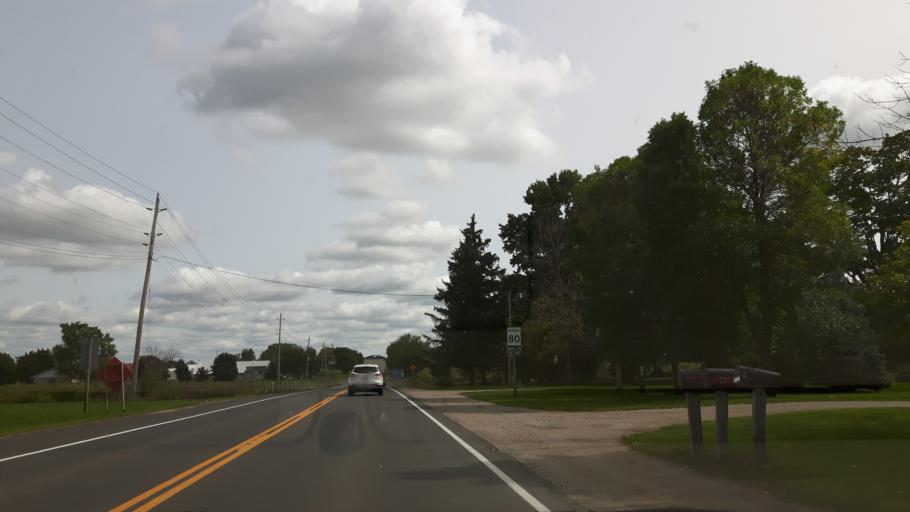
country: CA
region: Ontario
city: Bluewater
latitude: 43.6120
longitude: -81.5280
